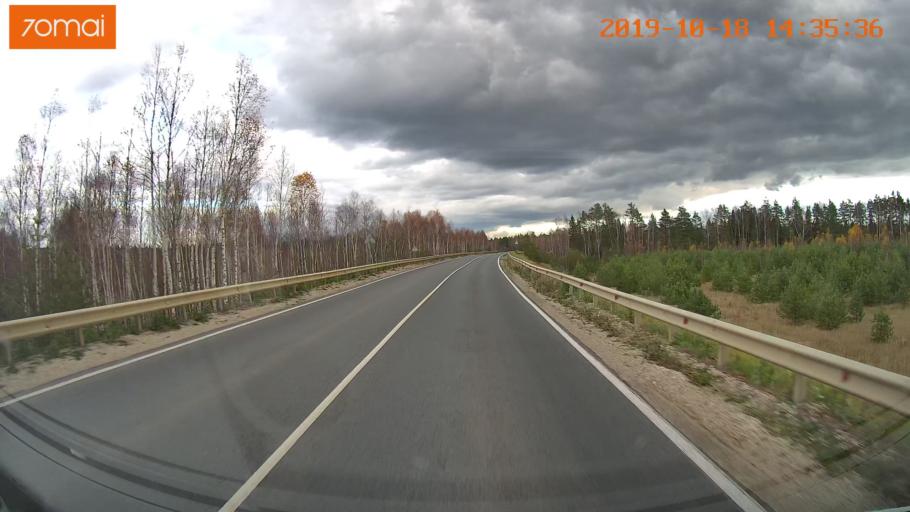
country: RU
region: Vladimir
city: Velikodvorskiy
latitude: 55.2225
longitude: 40.6414
